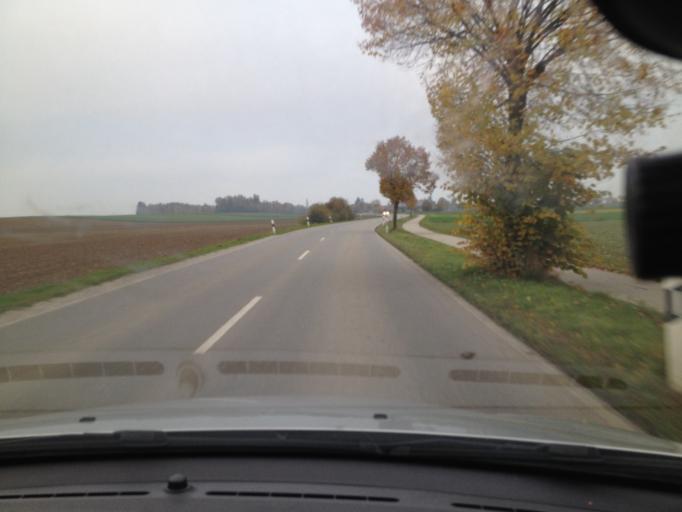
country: DE
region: Bavaria
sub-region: Swabia
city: Kleinaitingen
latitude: 48.2085
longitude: 10.8341
